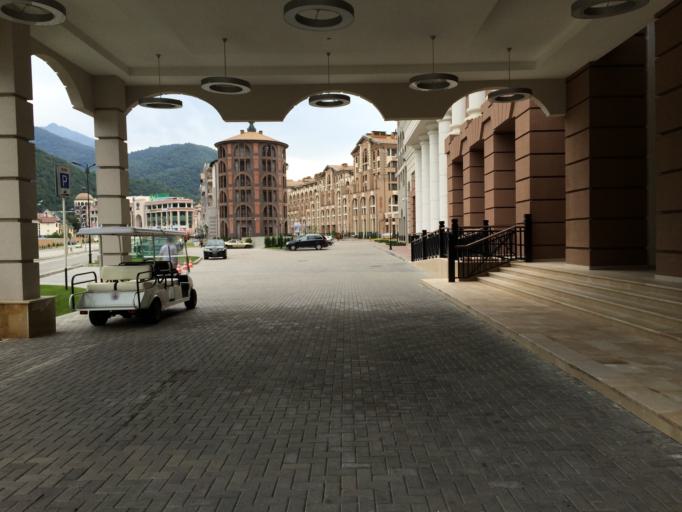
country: RU
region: Krasnodarskiy
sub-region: Sochi City
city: Krasnaya Polyana
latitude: 43.6839
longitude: 40.2568
